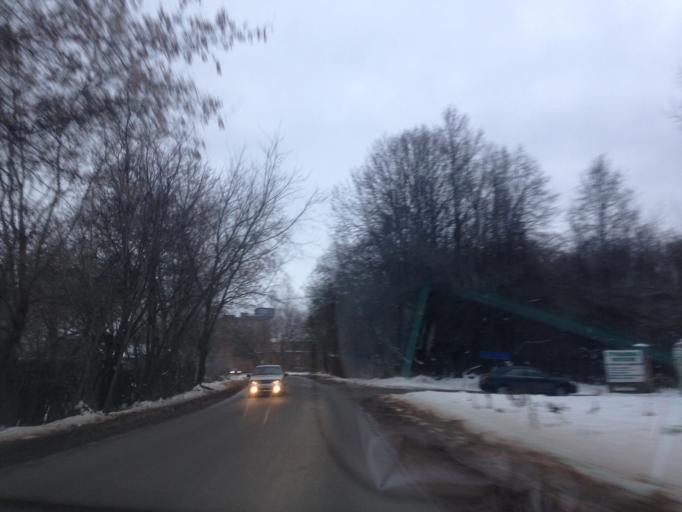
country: RU
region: Tula
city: Shchekino
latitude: 54.0218
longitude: 37.5145
